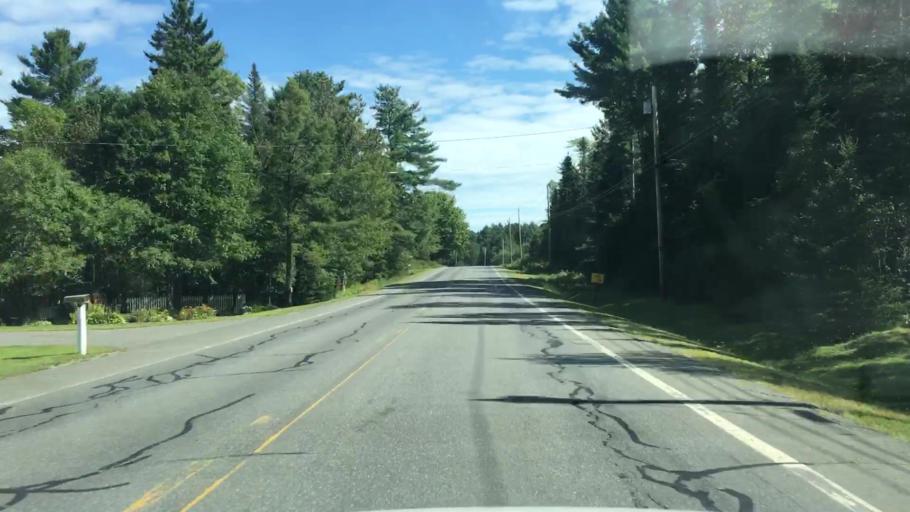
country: US
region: Maine
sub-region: Penobscot County
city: Garland
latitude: 45.0904
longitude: -69.2177
